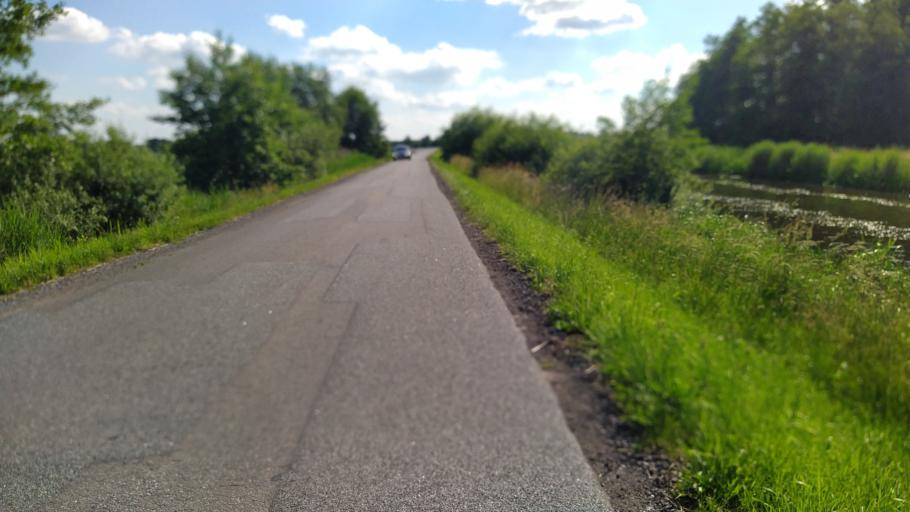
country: DE
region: Lower Saxony
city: Steinau
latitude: 53.6585
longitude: 8.8998
